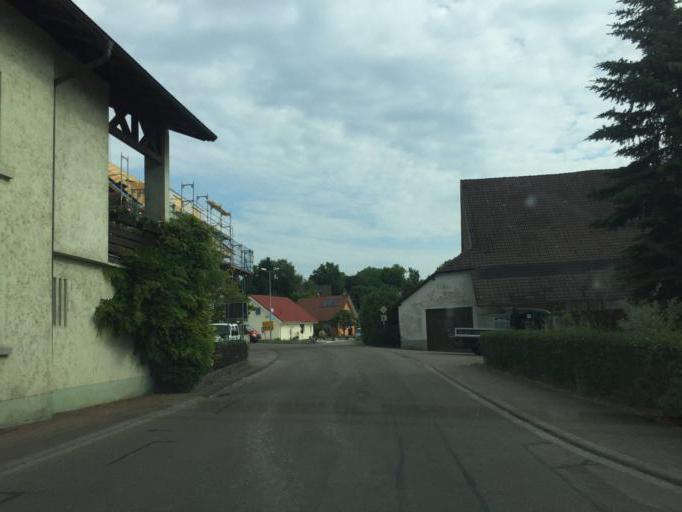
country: CH
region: Zurich
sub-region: Bezirk Andelfingen
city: Dachsen
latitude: 47.6572
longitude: 8.5993
